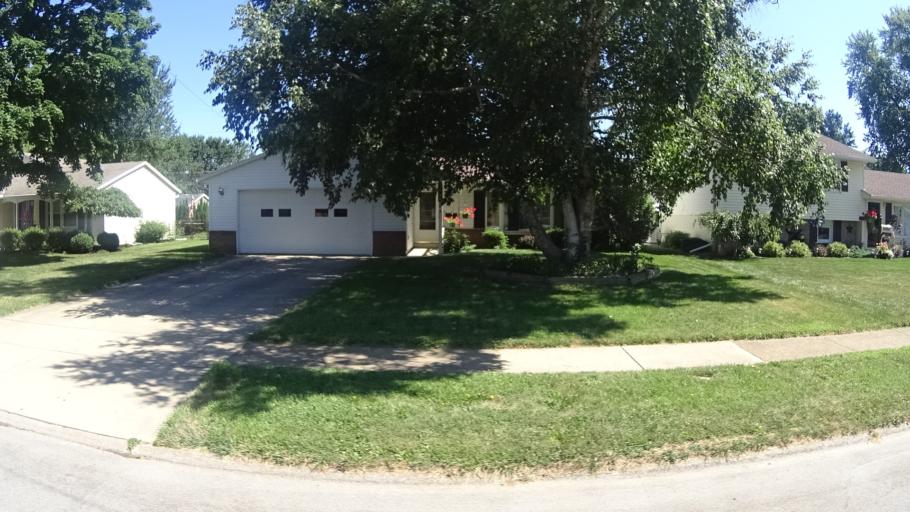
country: US
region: Ohio
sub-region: Erie County
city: Sandusky
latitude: 41.4269
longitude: -82.6536
